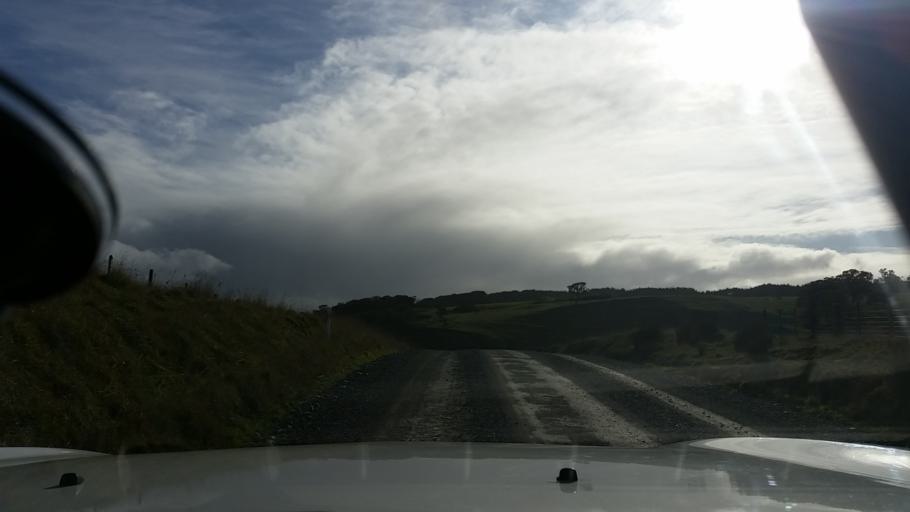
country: NZ
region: Chatham Islands
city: Waitangi
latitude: -43.8128
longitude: -176.5863
